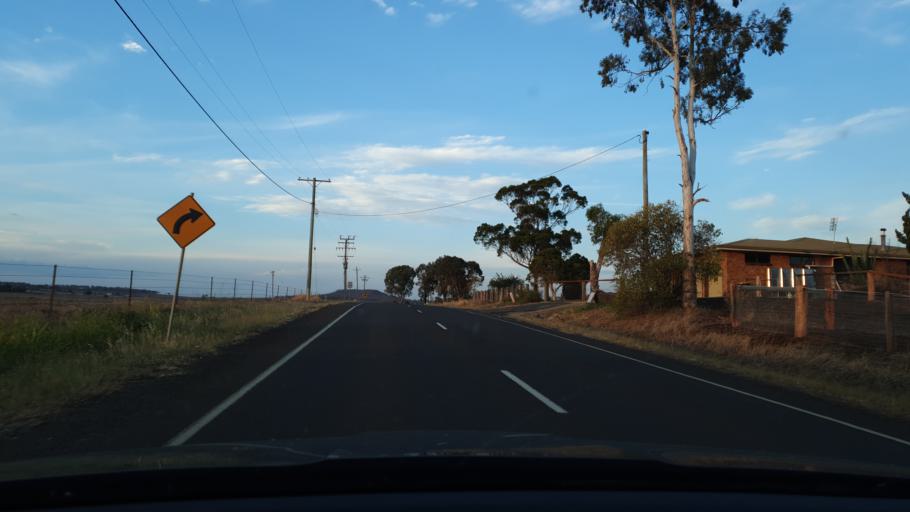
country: AU
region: Queensland
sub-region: Southern Downs
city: Warwick
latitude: -28.0276
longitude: 151.9830
